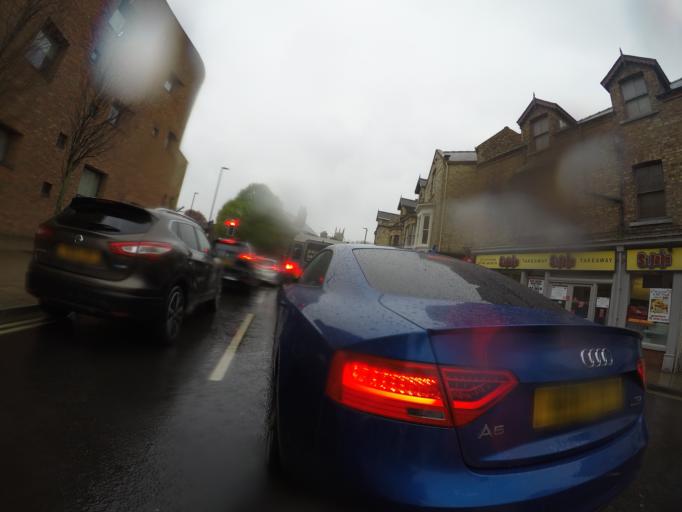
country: GB
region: England
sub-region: City of York
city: York
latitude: 53.9655
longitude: -1.0832
